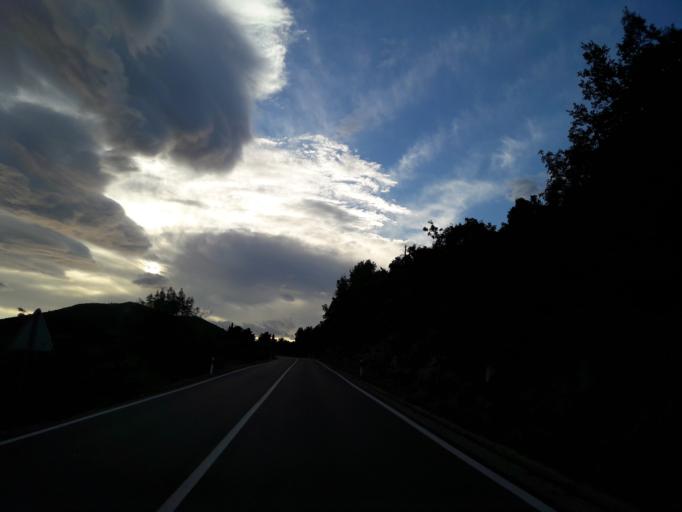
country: BA
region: Federation of Bosnia and Herzegovina
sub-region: Hercegovacko-Bosanski Kanton
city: Neum
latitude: 42.8878
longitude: 17.5021
